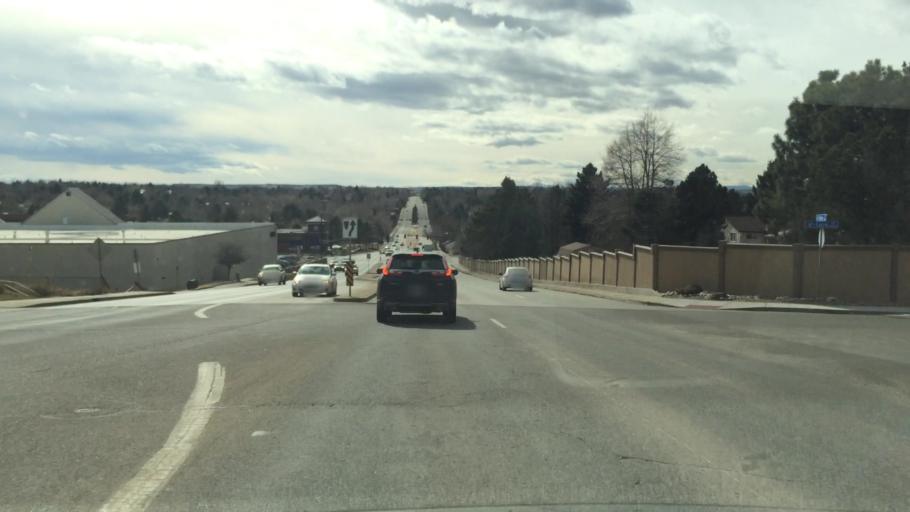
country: US
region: Colorado
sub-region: Arapahoe County
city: Castlewood
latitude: 39.5972
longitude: -104.9042
